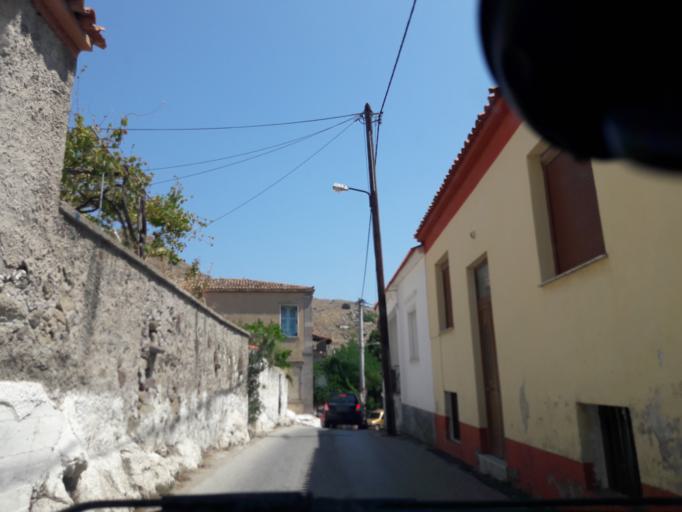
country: GR
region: North Aegean
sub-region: Nomos Lesvou
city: Myrina
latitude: 39.8559
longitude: 25.0863
